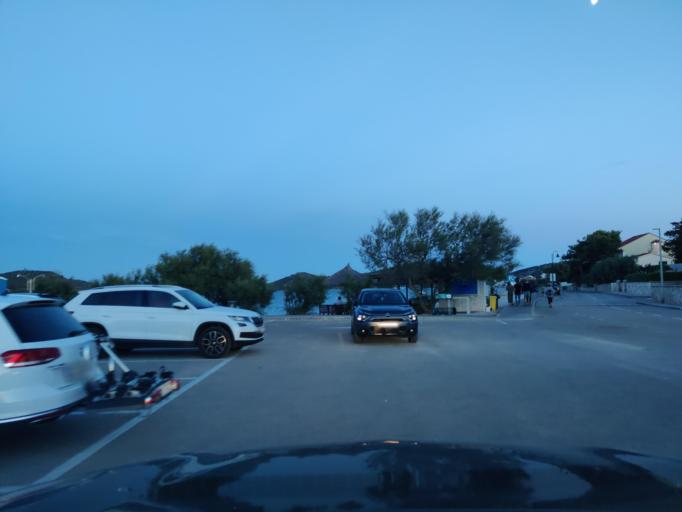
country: HR
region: Sibensko-Kniniska
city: Murter
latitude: 43.8195
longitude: 15.6051
